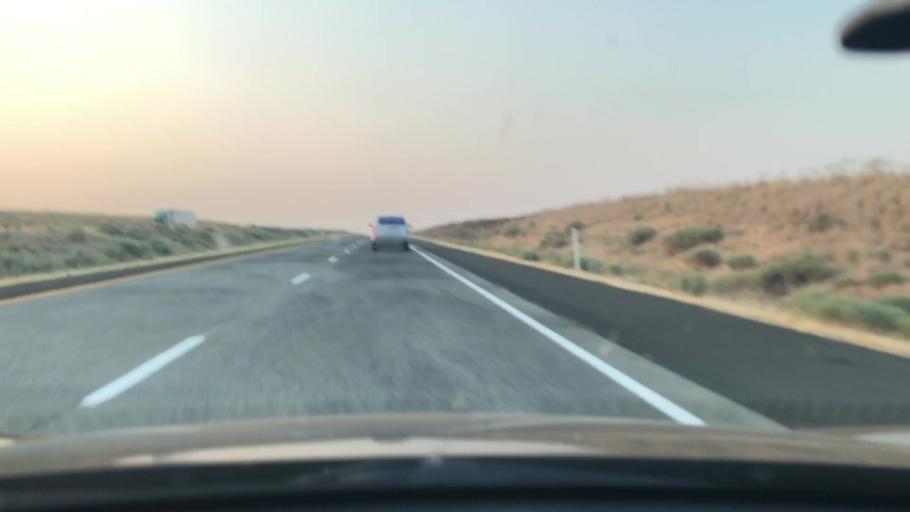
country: US
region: Washington
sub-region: Franklin County
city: Connell
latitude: 46.7082
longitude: -118.8360
